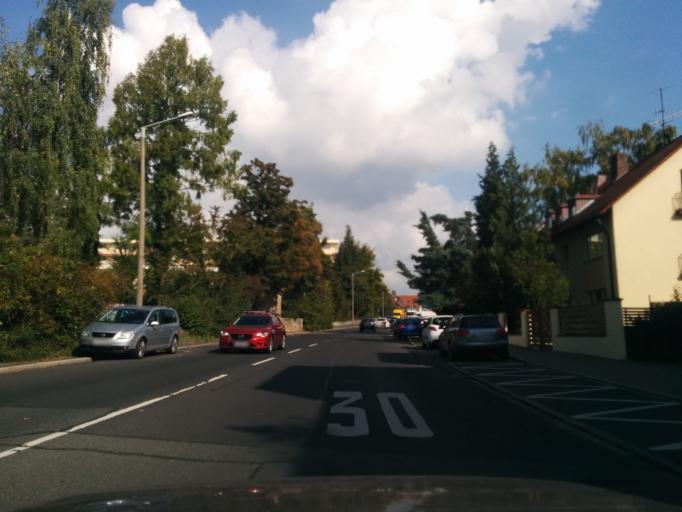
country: DE
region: Bavaria
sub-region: Regierungsbezirk Mittelfranken
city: Nuernberg
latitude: 49.4647
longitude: 11.1042
